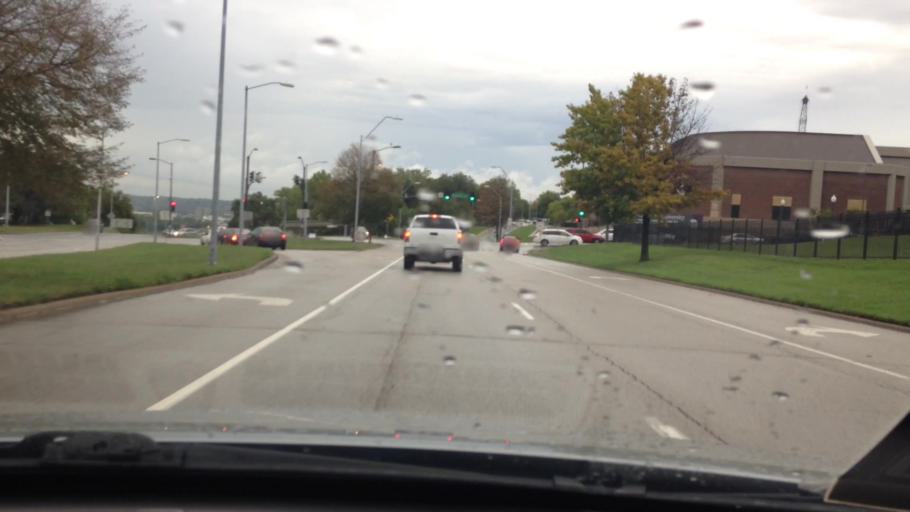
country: US
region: Missouri
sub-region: Jackson County
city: Kansas City
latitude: 39.1058
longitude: -94.5635
